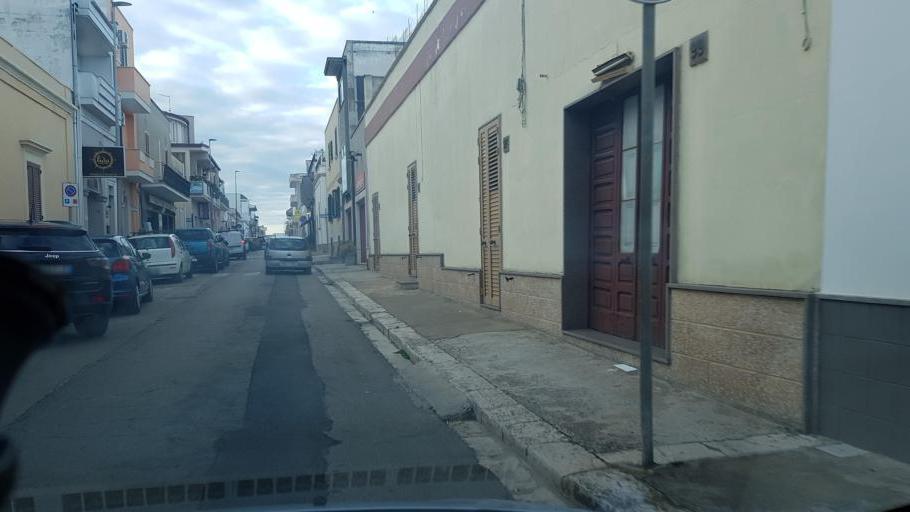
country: IT
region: Apulia
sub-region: Provincia di Lecce
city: Veglie
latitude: 40.3330
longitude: 17.9671
